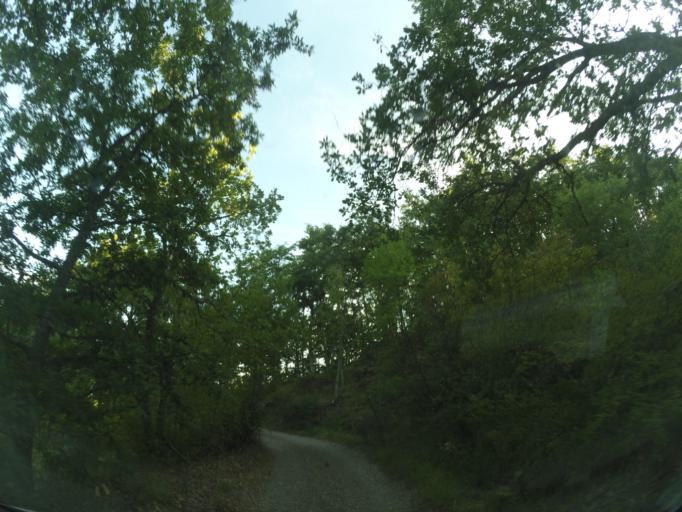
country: IT
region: Tuscany
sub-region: Province of Arezzo
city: Talla
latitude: 43.5625
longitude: 11.7845
